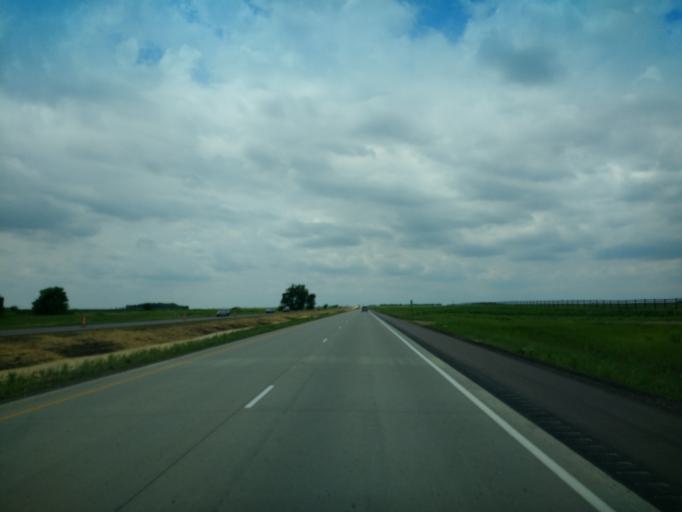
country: US
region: Minnesota
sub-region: Cottonwood County
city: Mountain Lake
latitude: 43.9231
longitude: -94.9837
